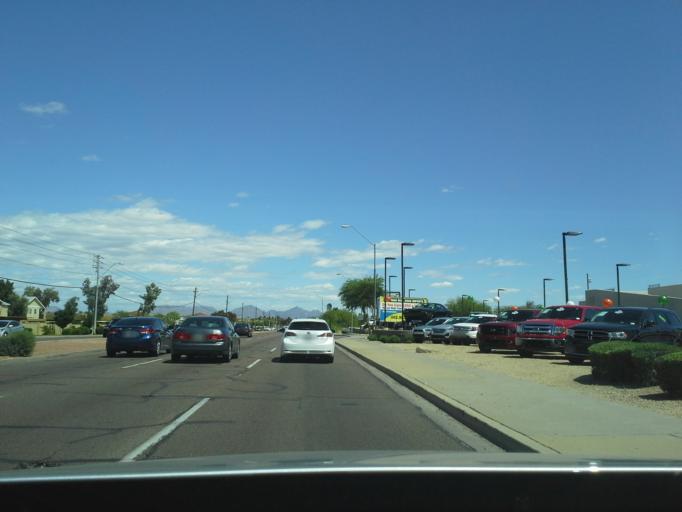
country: US
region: Arizona
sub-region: Maricopa County
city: Glendale
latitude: 33.6401
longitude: -112.0867
